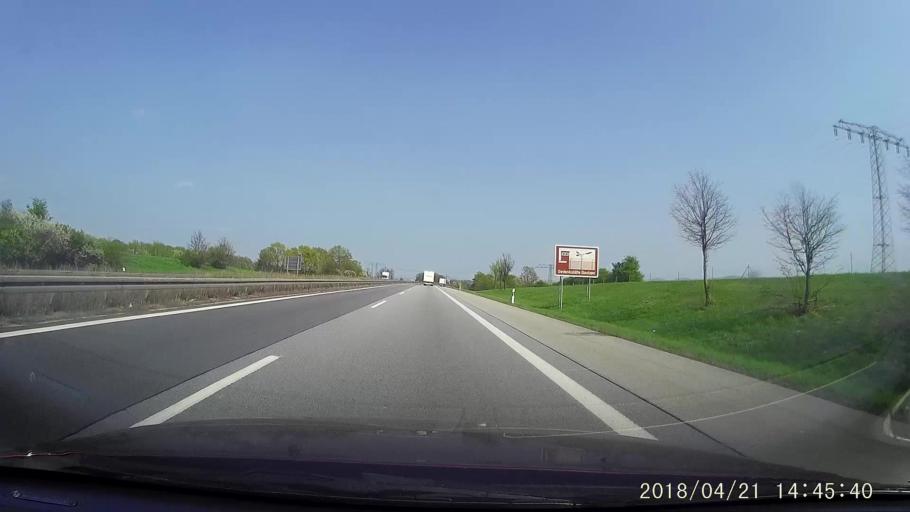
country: DE
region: Saxony
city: Bautzen
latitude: 51.1885
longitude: 14.3804
